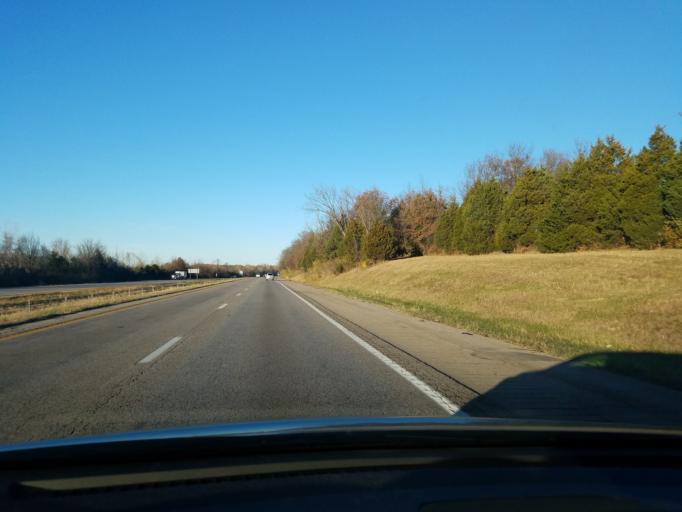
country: US
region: Missouri
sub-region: Franklin County
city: Saint Clair
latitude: 38.3721
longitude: -90.9722
